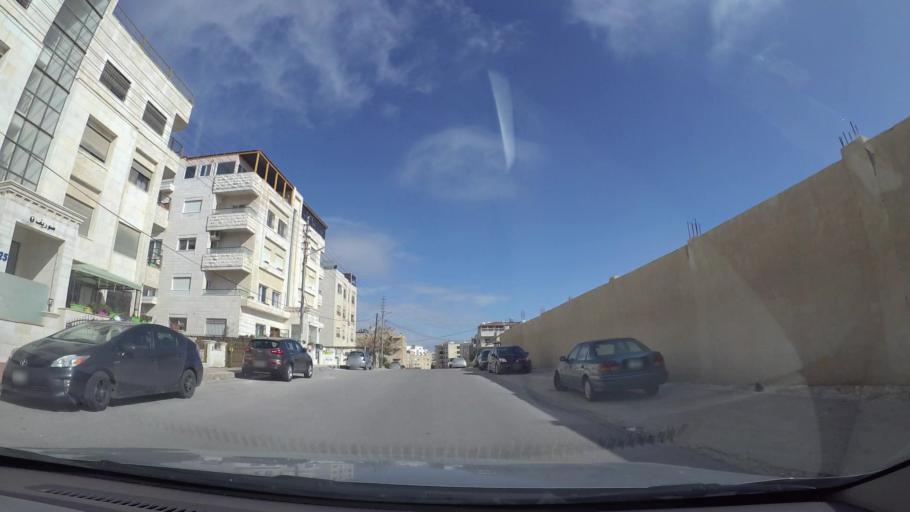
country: JO
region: Amman
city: Al Jubayhah
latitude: 32.0049
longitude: 35.8488
